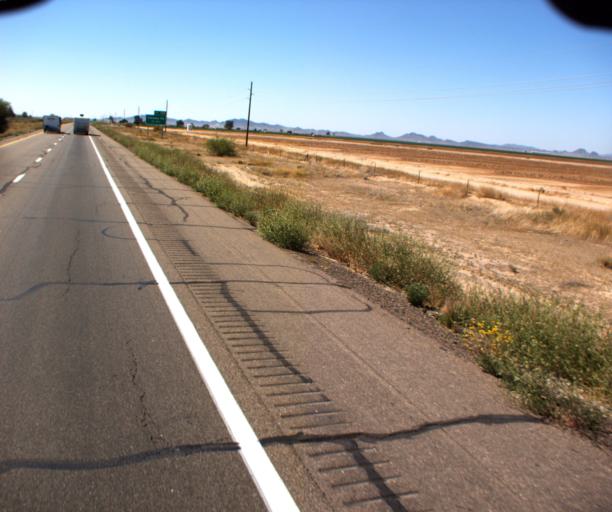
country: US
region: Arizona
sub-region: Maricopa County
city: Gila Bend
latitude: 32.9238
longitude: -112.8740
